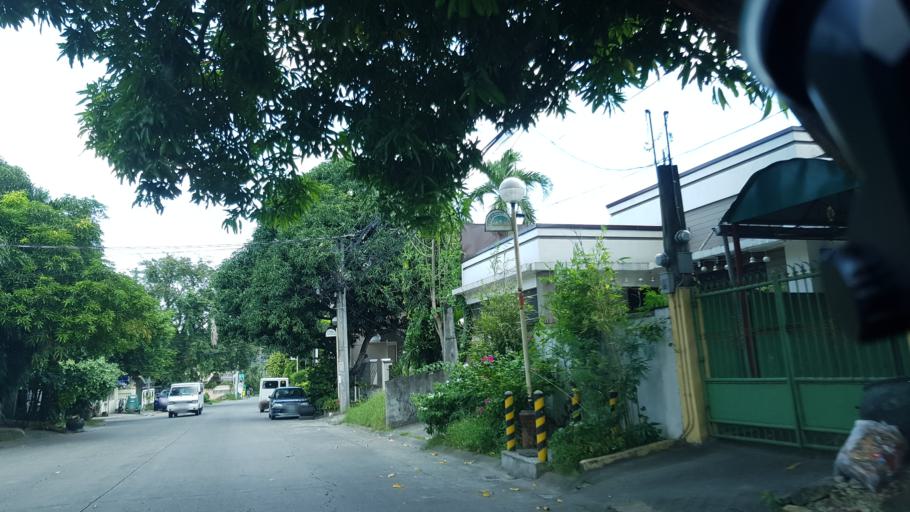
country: PH
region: Calabarzon
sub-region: Province of Rizal
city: Las Pinas
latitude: 14.4315
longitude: 120.9875
